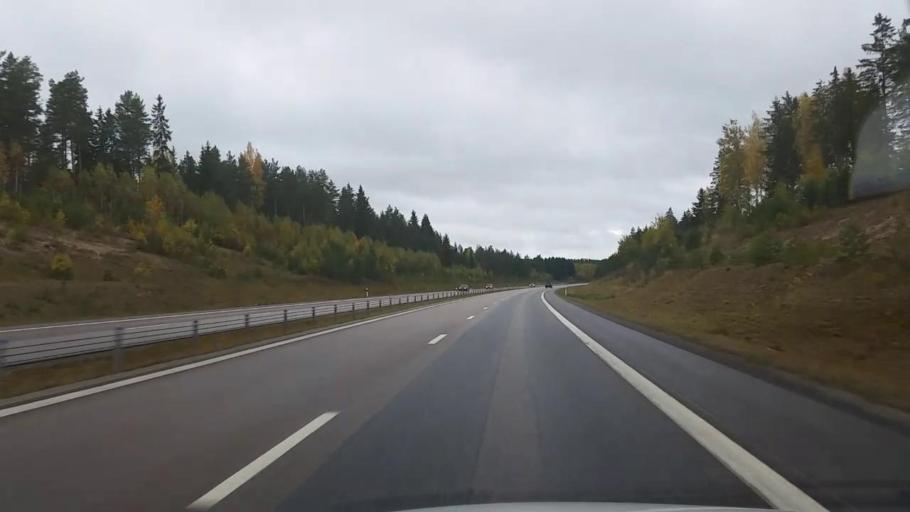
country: SE
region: Uppsala
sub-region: Osthammars Kommun
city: Bjorklinge
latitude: 60.1206
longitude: 17.5474
